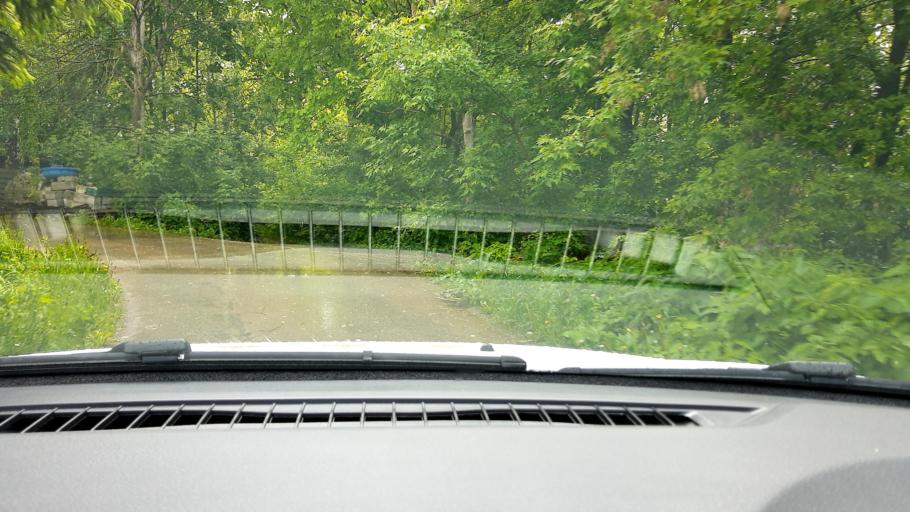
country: RU
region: Nizjnij Novgorod
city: Afonino
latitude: 56.2924
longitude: 44.0851
